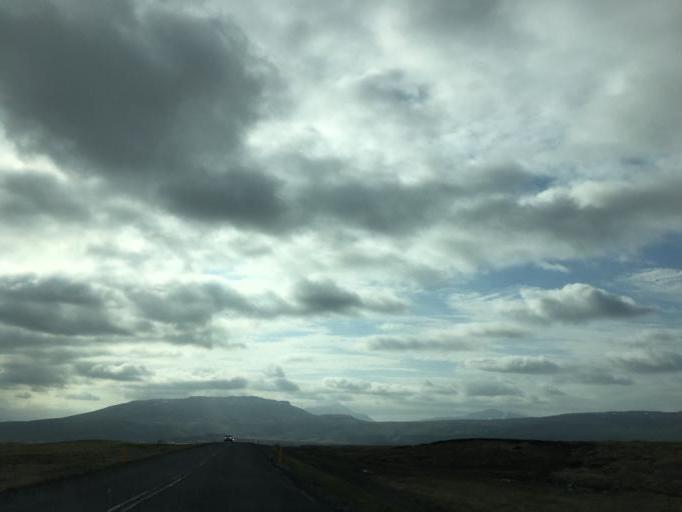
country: IS
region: South
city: Vestmannaeyjar
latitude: 64.3061
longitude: -20.1873
